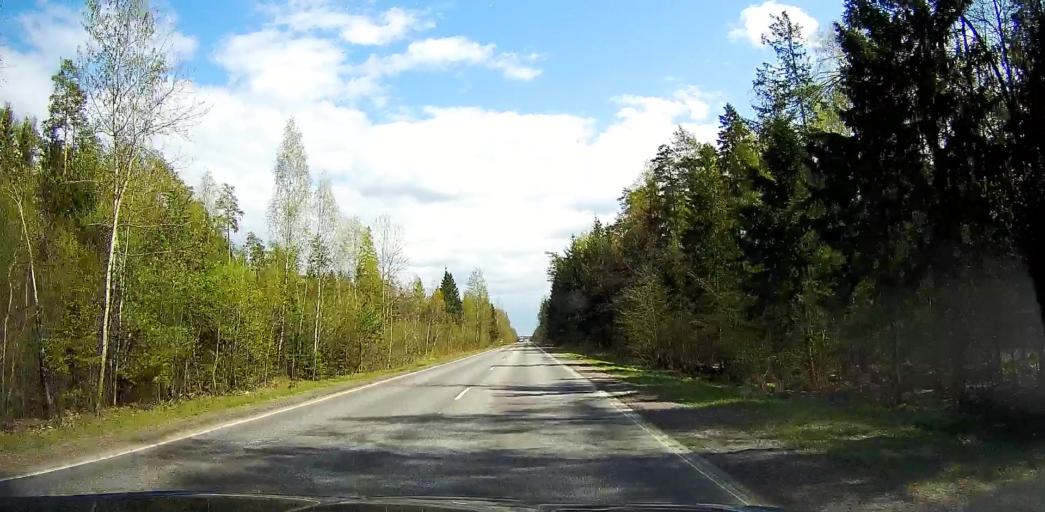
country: RU
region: Moskovskaya
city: Davydovo
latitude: 55.5514
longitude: 38.7744
